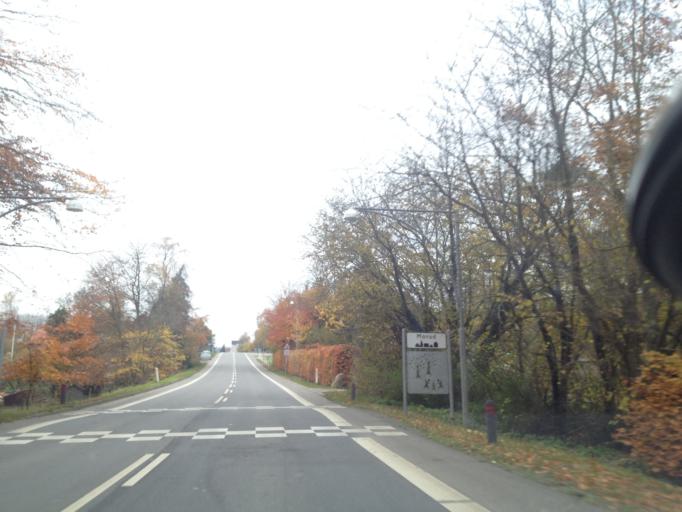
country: DK
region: South Denmark
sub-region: Nordfyns Kommune
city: Sonderso
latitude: 55.4434
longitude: 10.1977
